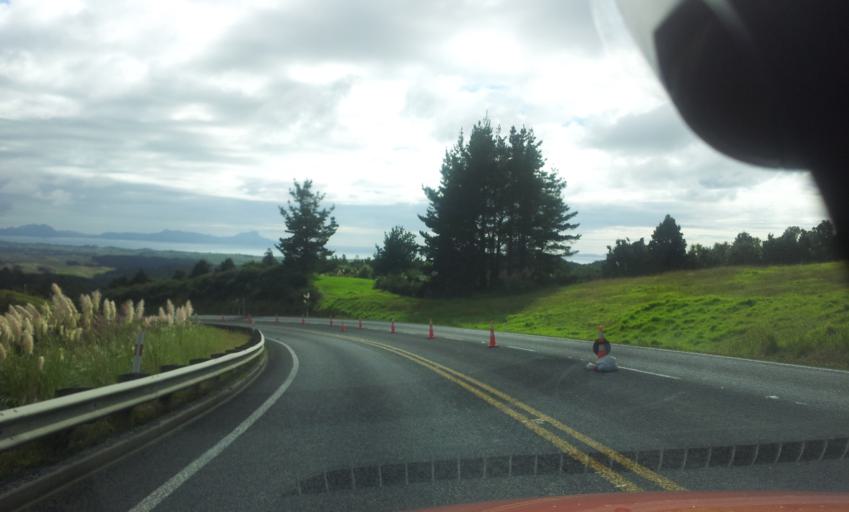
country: NZ
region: Northland
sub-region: Whangarei
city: Ruakaka
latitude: -36.0611
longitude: 174.4263
